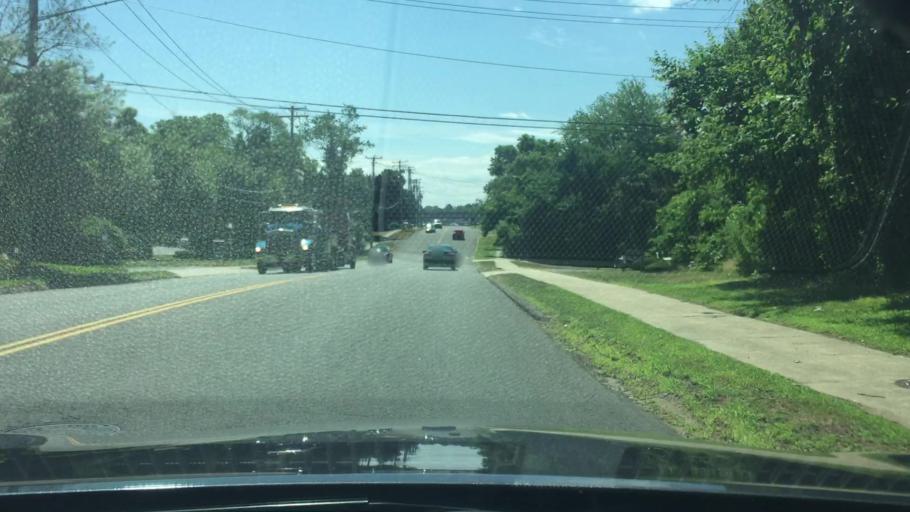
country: US
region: Connecticut
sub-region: New Haven County
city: Milford
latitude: 41.2421
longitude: -73.0268
